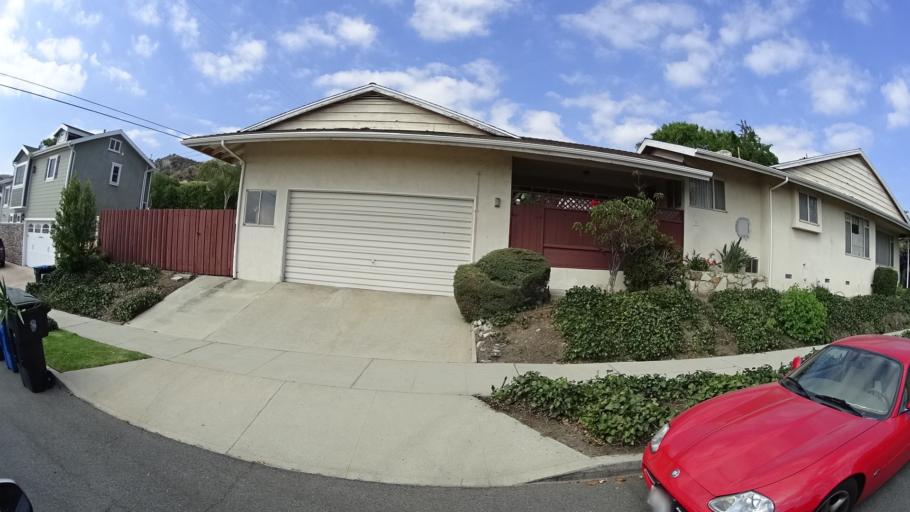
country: US
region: California
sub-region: Los Angeles County
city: Burbank
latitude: 34.1969
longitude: -118.3081
